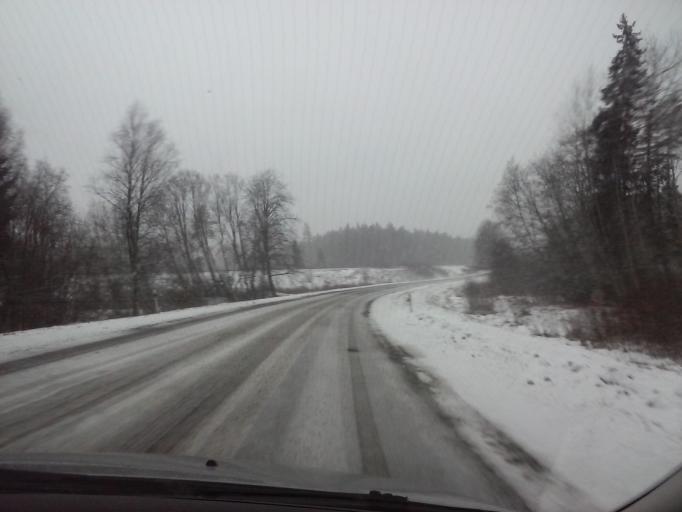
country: LV
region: Valkas Rajons
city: Valka
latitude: 57.7165
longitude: 25.9327
